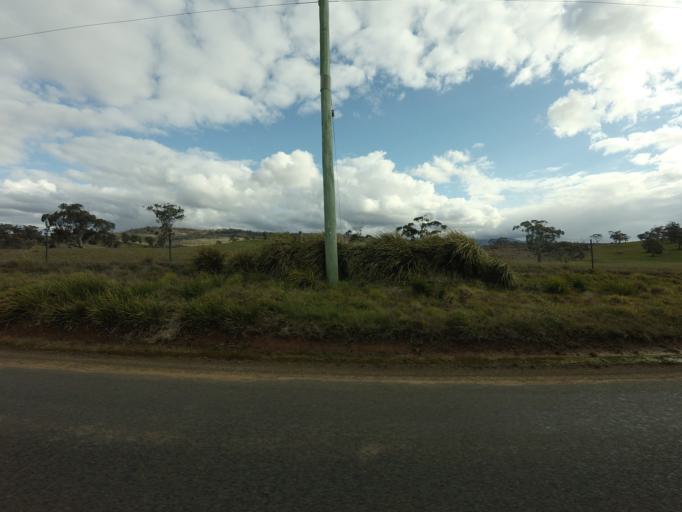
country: AU
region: Tasmania
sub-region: Northern Midlands
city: Evandale
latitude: -41.8829
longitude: 147.3097
